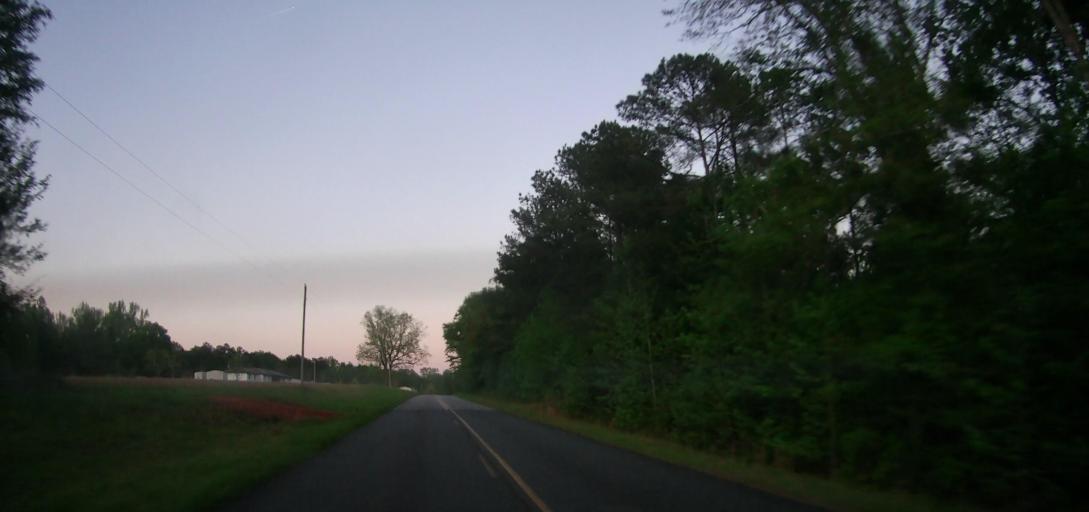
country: US
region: Georgia
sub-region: Marion County
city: Buena Vista
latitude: 32.2564
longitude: -84.6020
